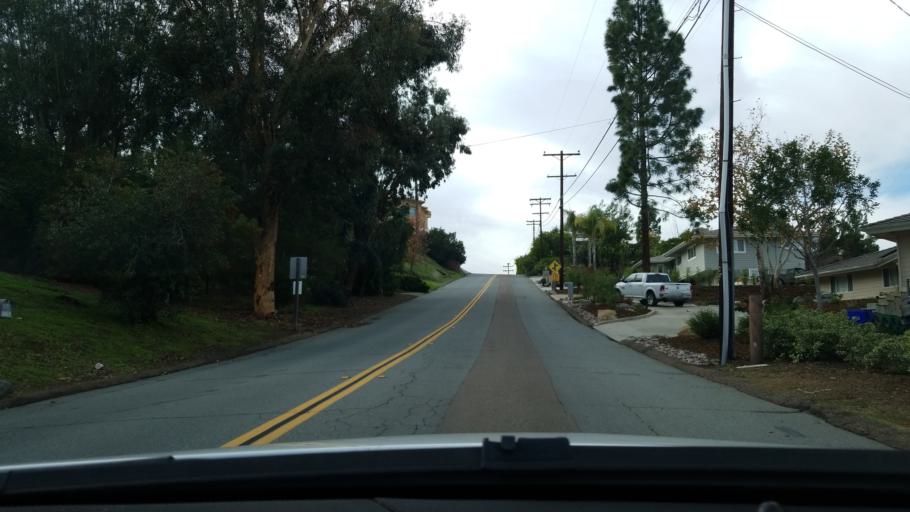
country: US
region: California
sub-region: San Diego County
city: Casa de Oro-Mount Helix
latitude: 32.7722
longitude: -116.9461
